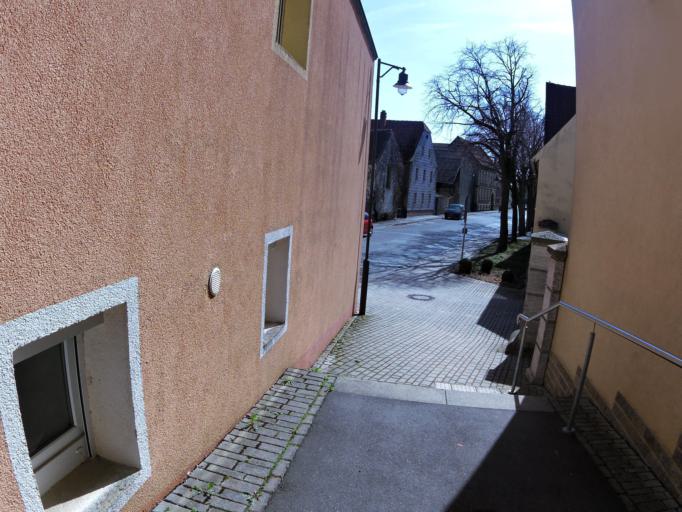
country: DE
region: Bavaria
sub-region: Regierungsbezirk Unterfranken
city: Biebelried
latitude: 49.7984
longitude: 10.1061
